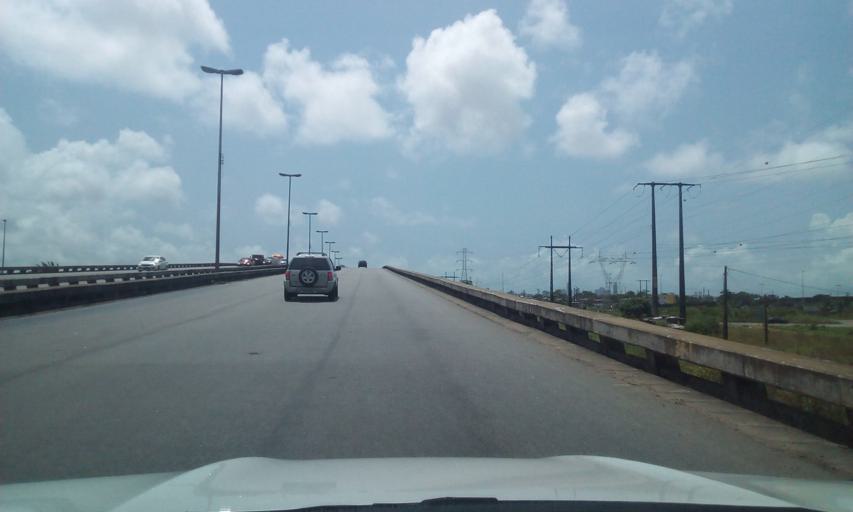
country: BR
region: Pernambuco
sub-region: Recife
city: Recife
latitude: -8.0677
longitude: -34.9443
